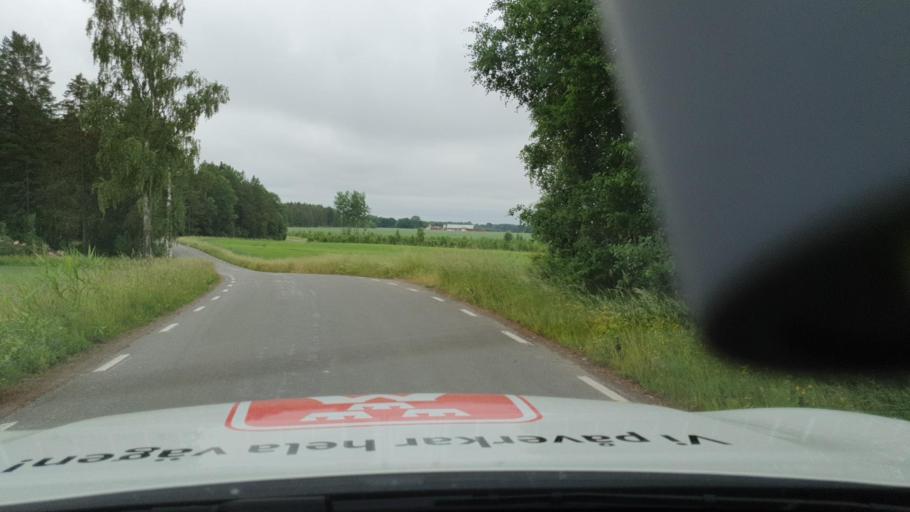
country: SE
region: Vaestra Goetaland
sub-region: Tidaholms Kommun
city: Olofstorp
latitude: 58.3850
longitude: 13.9982
